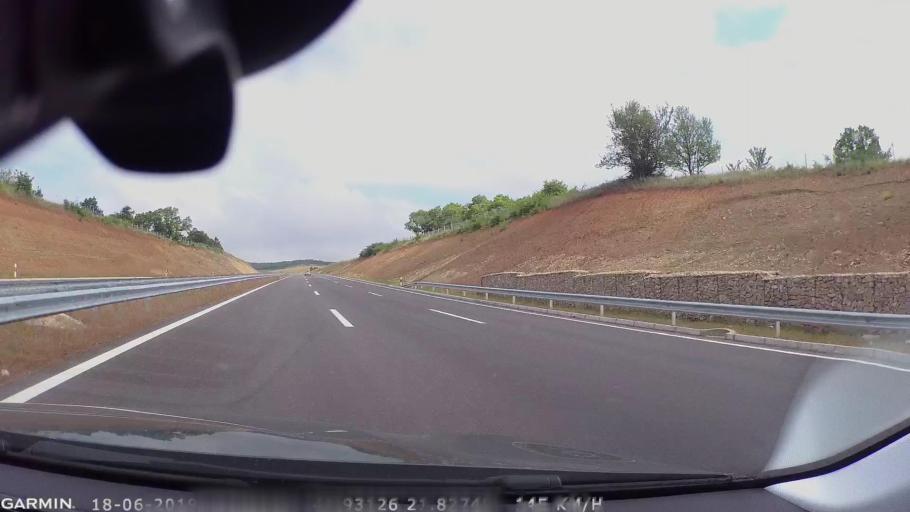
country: MK
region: Sveti Nikole
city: Gorobinci
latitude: 41.9176
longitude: 21.8767
